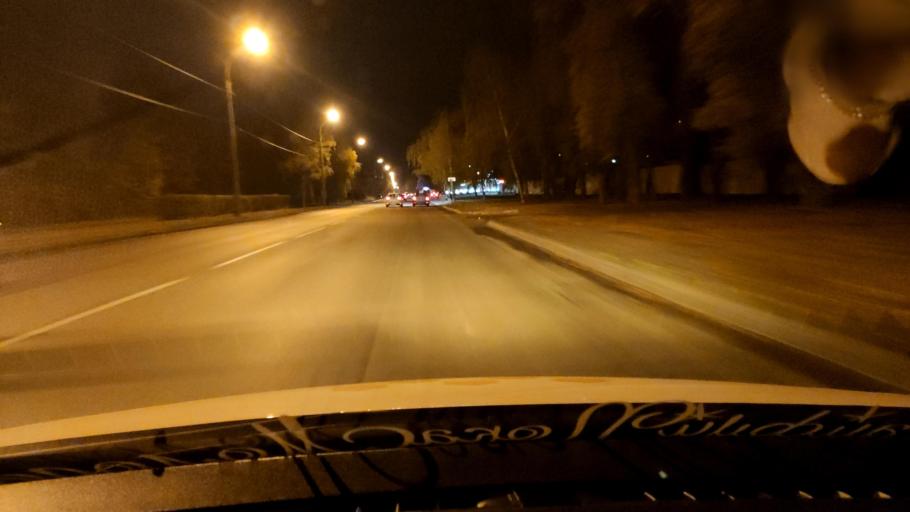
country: RU
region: Voronezj
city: Voronezh
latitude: 51.6492
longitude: 39.2113
